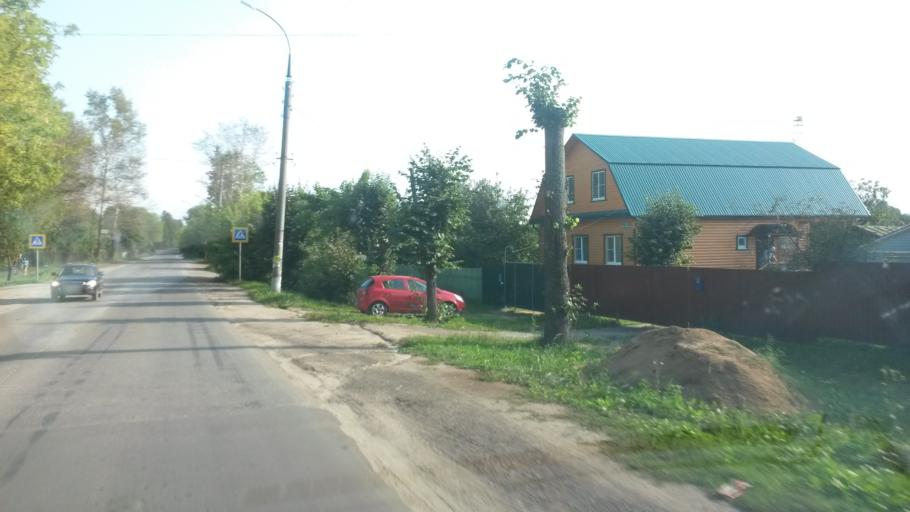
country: RU
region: Jaroslavl
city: Petrovsk
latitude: 57.0091
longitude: 39.2693
